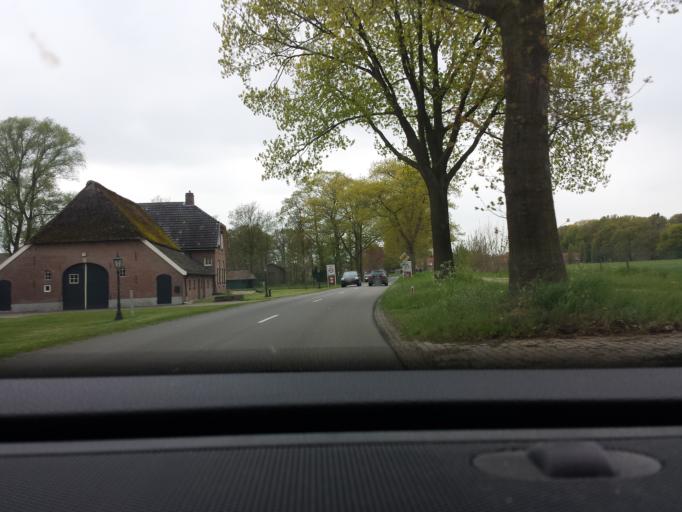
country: NL
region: Gelderland
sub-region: Gemeente Bronckhorst
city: Hengelo
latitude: 52.0565
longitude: 6.3269
